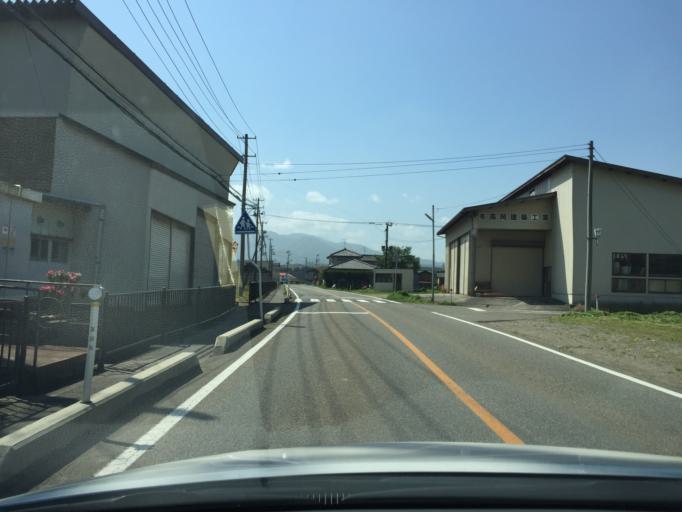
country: JP
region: Niigata
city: Muramatsu
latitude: 37.6860
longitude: 139.1516
